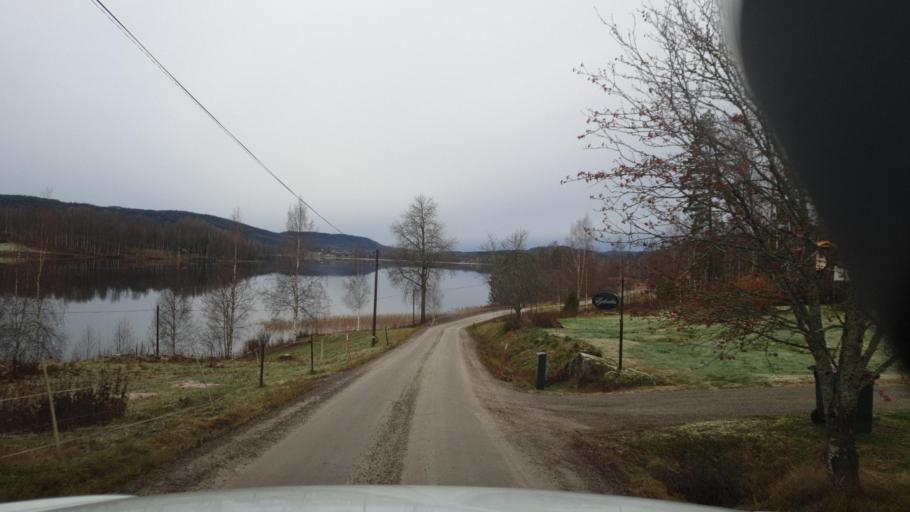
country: SE
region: Vaermland
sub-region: Arvika Kommun
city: Arvika
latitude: 59.7194
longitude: 12.8384
